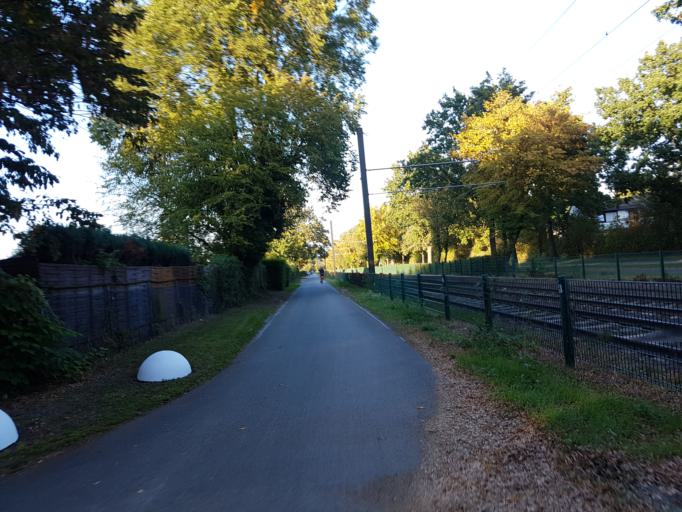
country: DE
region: Lower Saxony
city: Langenhagen
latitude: 52.4151
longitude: 9.7523
